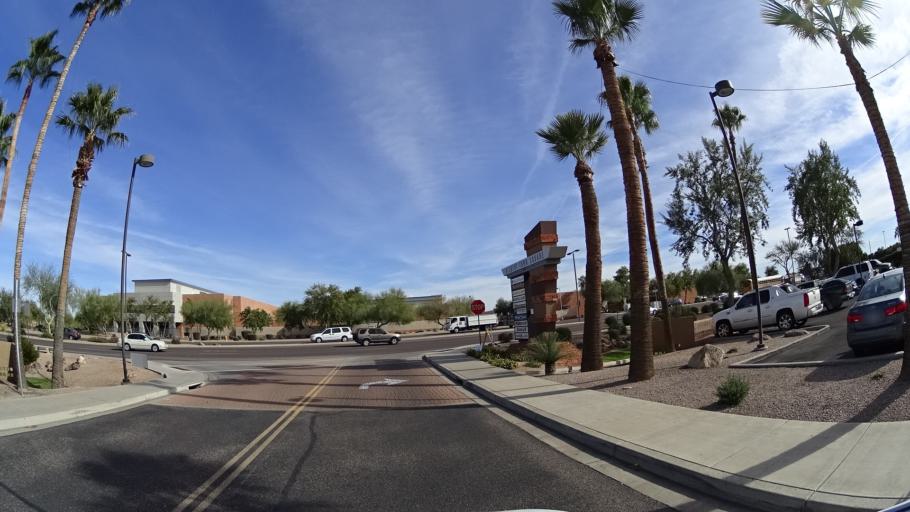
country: US
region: Arizona
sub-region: Maricopa County
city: Gilbert
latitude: 33.3294
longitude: -111.7904
